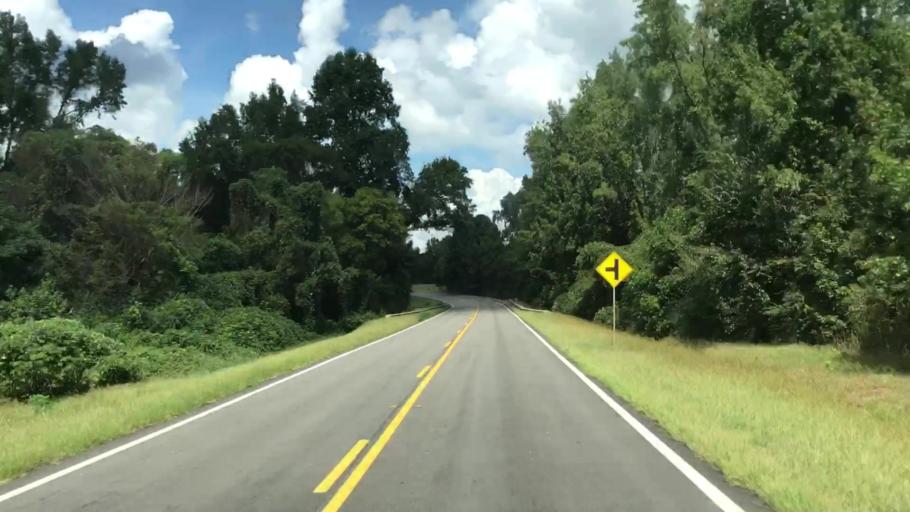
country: US
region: Georgia
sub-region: Greene County
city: Union Point
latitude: 33.5484
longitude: -83.0979
